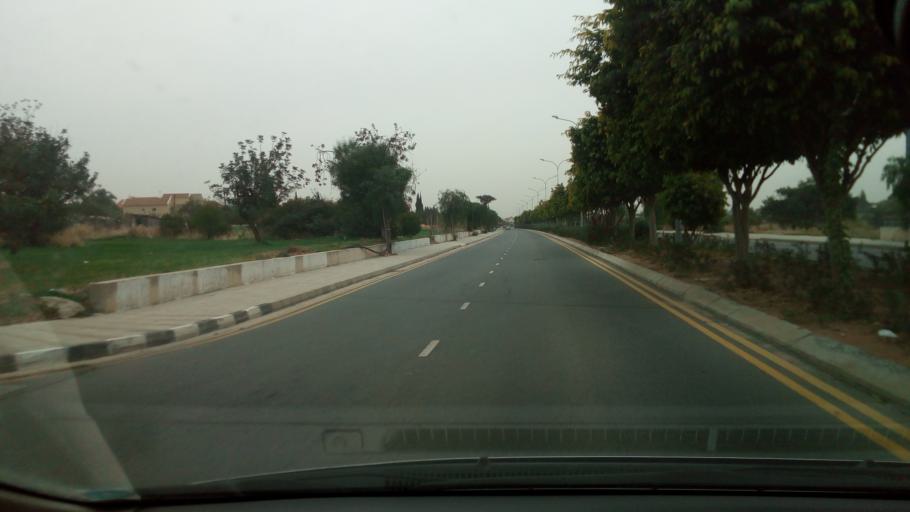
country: CY
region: Limassol
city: Pano Polemidia
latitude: 34.7085
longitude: 33.0006
